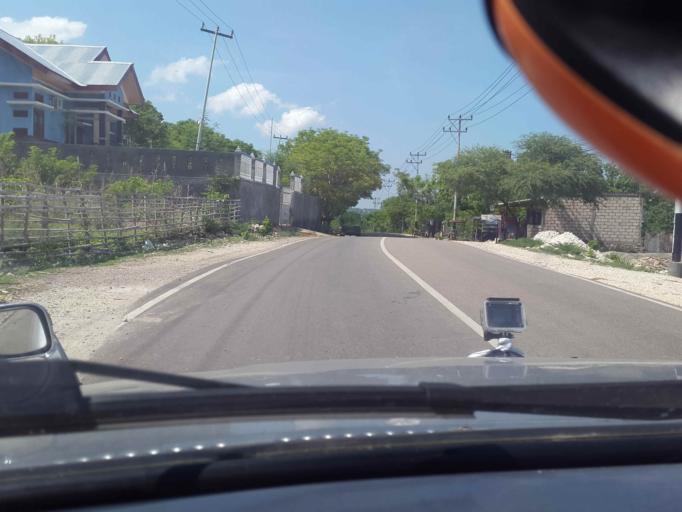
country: ID
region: East Nusa Tenggara
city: Alak
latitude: -10.2040
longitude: 123.5310
